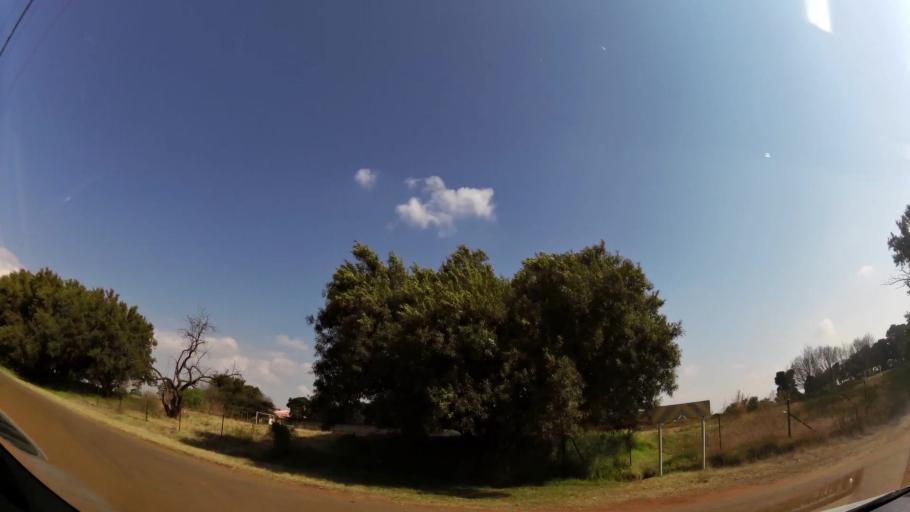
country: ZA
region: Gauteng
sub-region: Ekurhuleni Metropolitan Municipality
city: Springs
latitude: -26.1800
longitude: 28.5339
